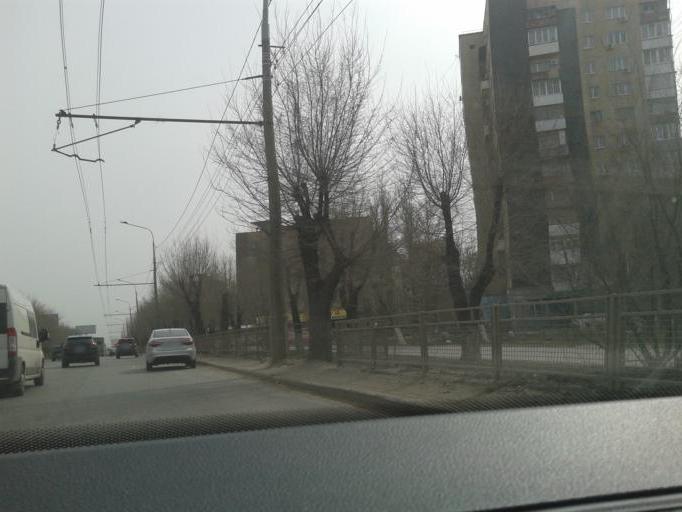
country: RU
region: Volgograd
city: Volgograd
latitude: 48.7409
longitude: 44.4908
